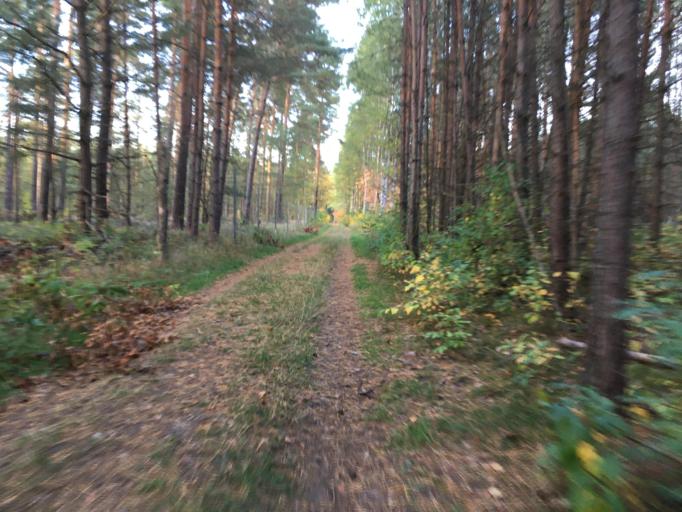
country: DE
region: Brandenburg
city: Birkenwerder
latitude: 52.7060
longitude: 13.3322
